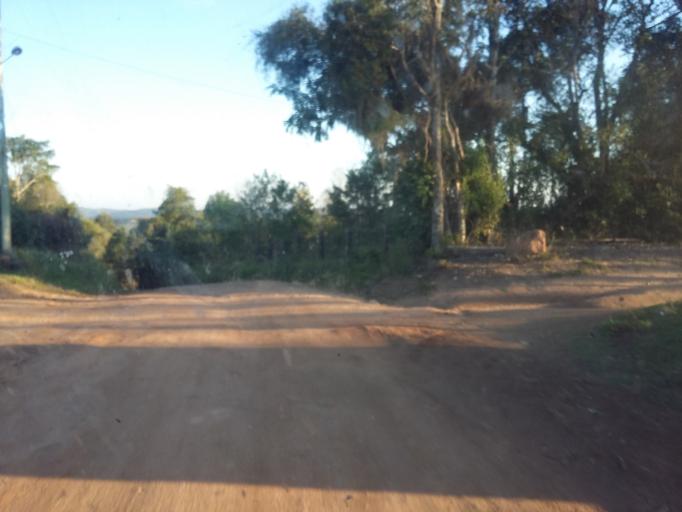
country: BR
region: Rio Grande do Sul
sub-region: Camaqua
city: Camaqua
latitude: -30.7174
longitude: -51.7701
